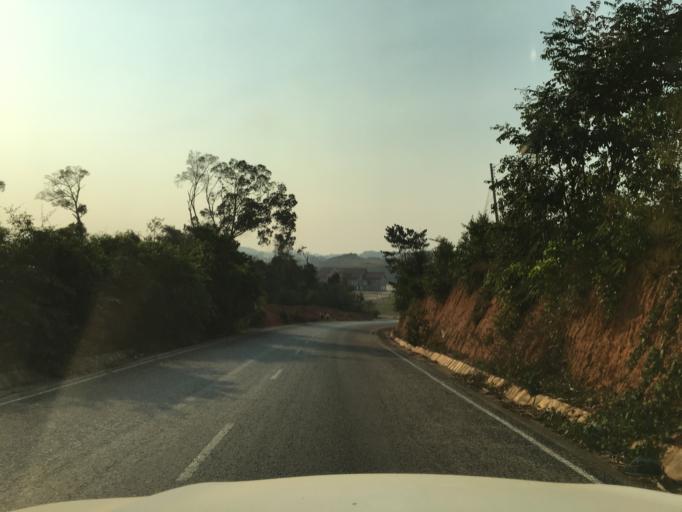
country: LA
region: Houaphan
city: Xam Nua
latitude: 20.6093
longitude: 104.0733
